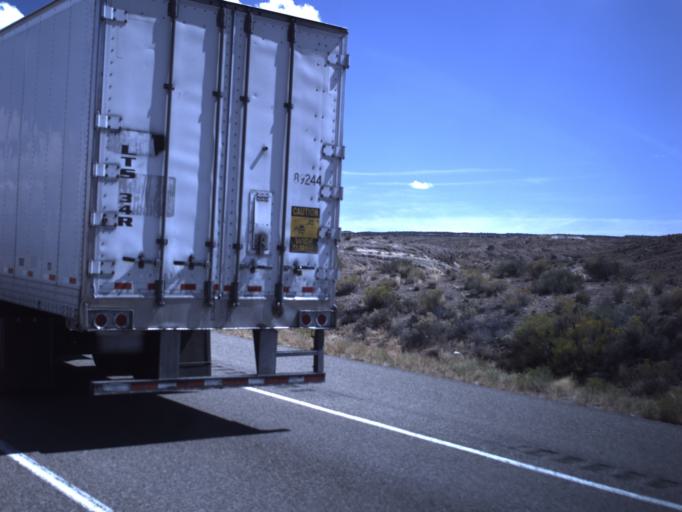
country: US
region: Utah
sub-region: Emery County
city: Ferron
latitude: 38.8463
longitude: -110.9957
